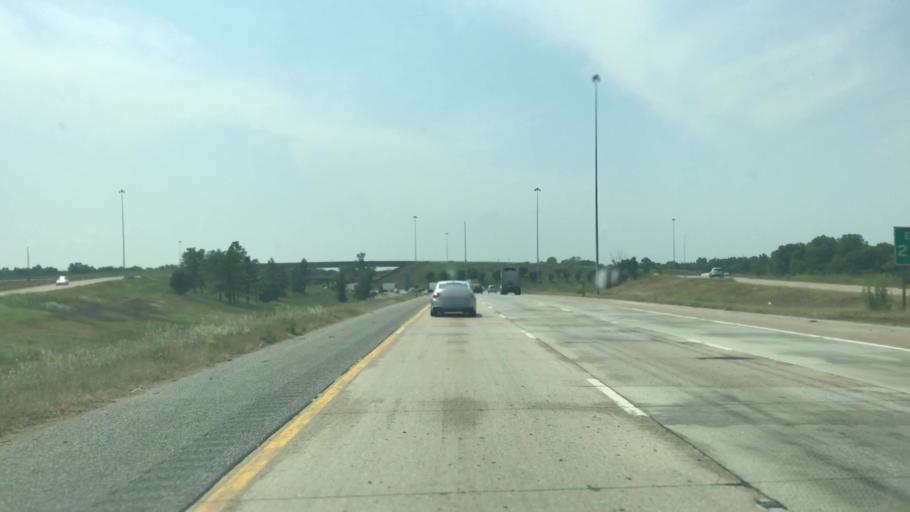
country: US
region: Tennessee
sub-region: Shelby County
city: Memphis
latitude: 35.1918
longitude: -90.0107
